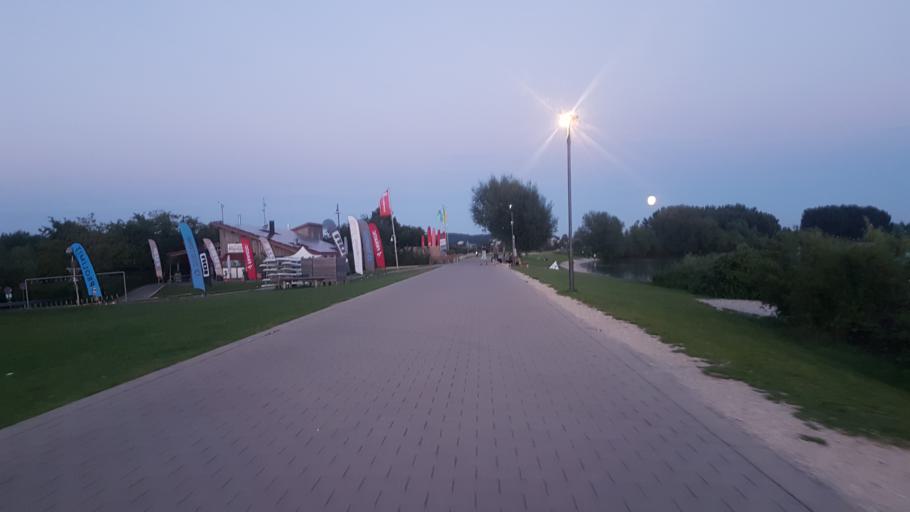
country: DE
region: Bavaria
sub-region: Regierungsbezirk Mittelfranken
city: Muhr am See
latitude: 49.1313
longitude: 10.7341
